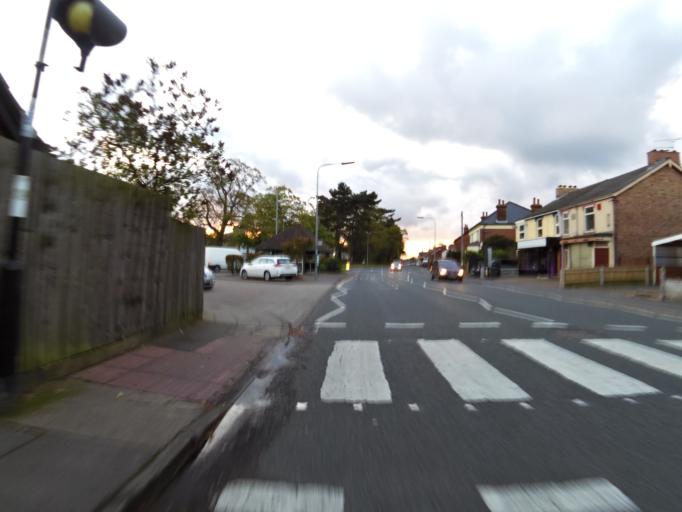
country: GB
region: England
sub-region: Suffolk
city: Ipswich
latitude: 52.0448
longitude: 1.1801
